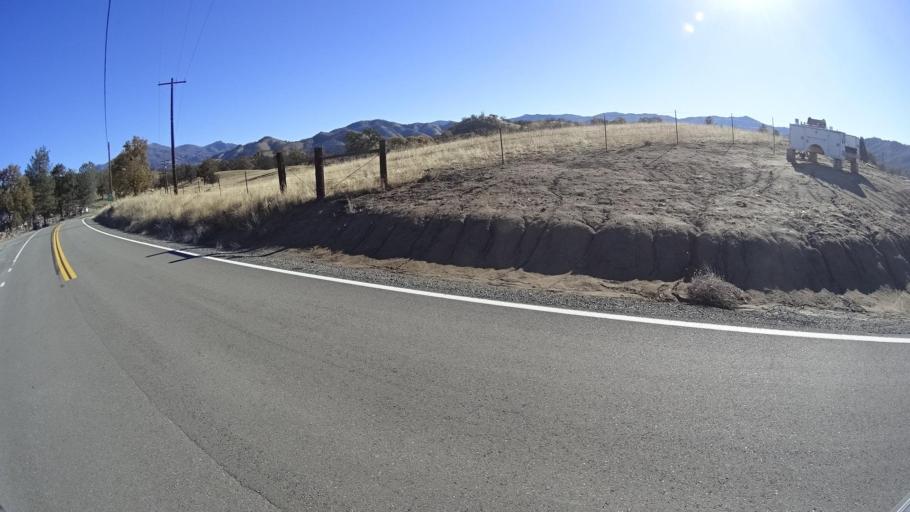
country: US
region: California
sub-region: Kern County
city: Alta Sierra
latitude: 35.7253
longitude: -118.7222
